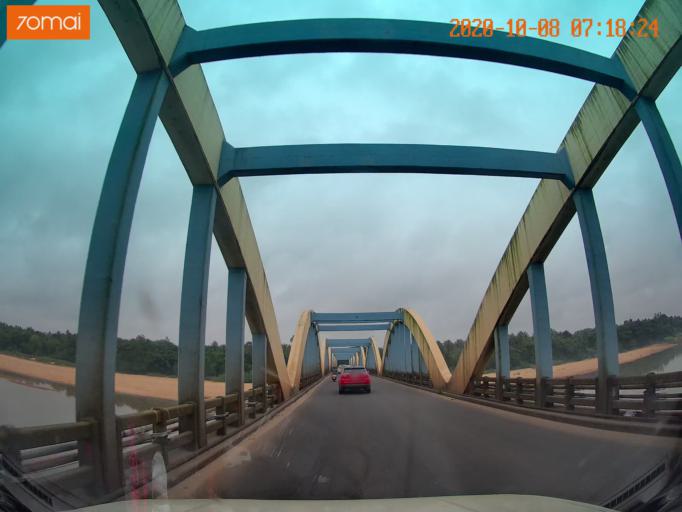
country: IN
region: Kerala
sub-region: Malappuram
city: Ponnani
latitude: 10.8405
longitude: 76.0237
